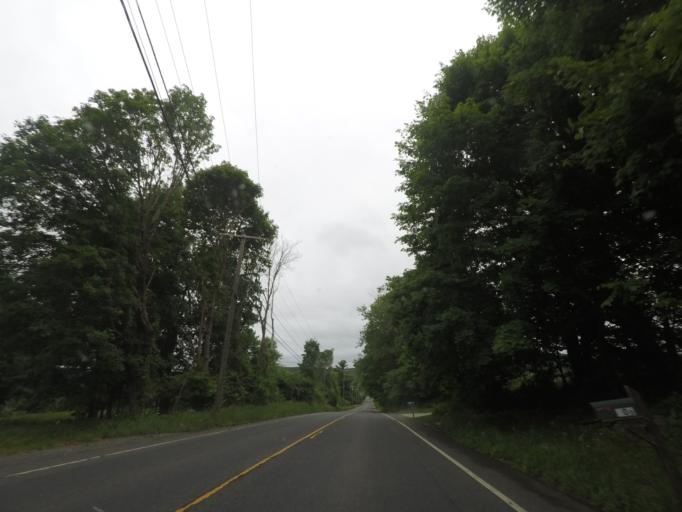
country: US
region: Connecticut
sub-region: Litchfield County
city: Canaan
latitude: 41.9328
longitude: -73.4245
